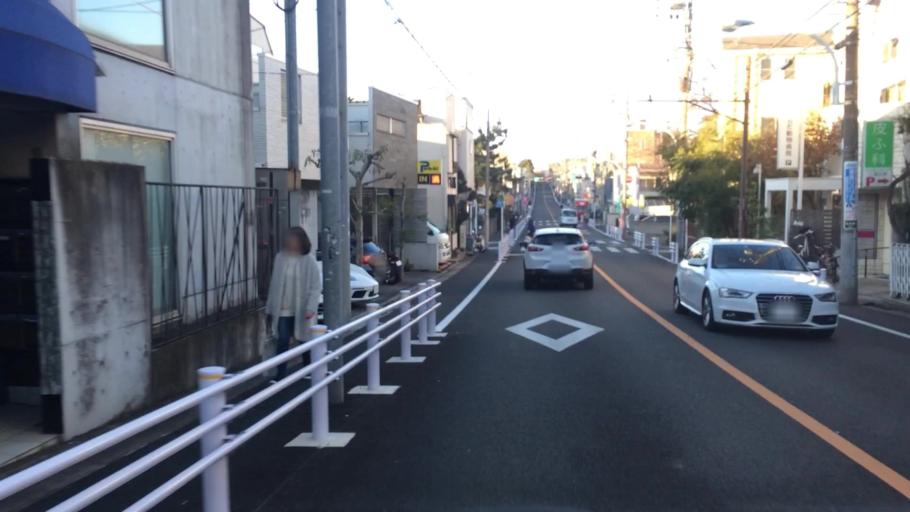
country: JP
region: Tokyo
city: Tokyo
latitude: 35.6161
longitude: 139.6692
